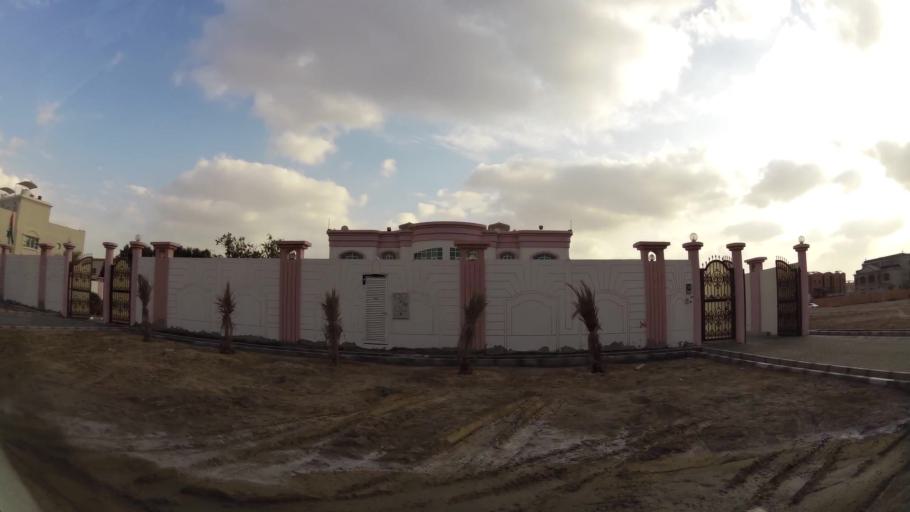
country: AE
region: Abu Dhabi
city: Abu Dhabi
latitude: 24.3669
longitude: 54.5503
